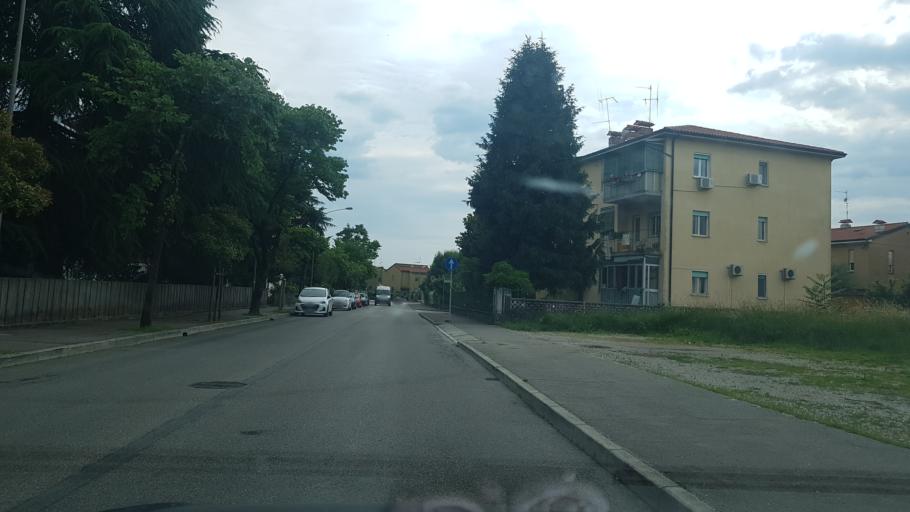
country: IT
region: Friuli Venezia Giulia
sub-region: Provincia di Gorizia
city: Gorizia
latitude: 45.9304
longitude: 13.6165
